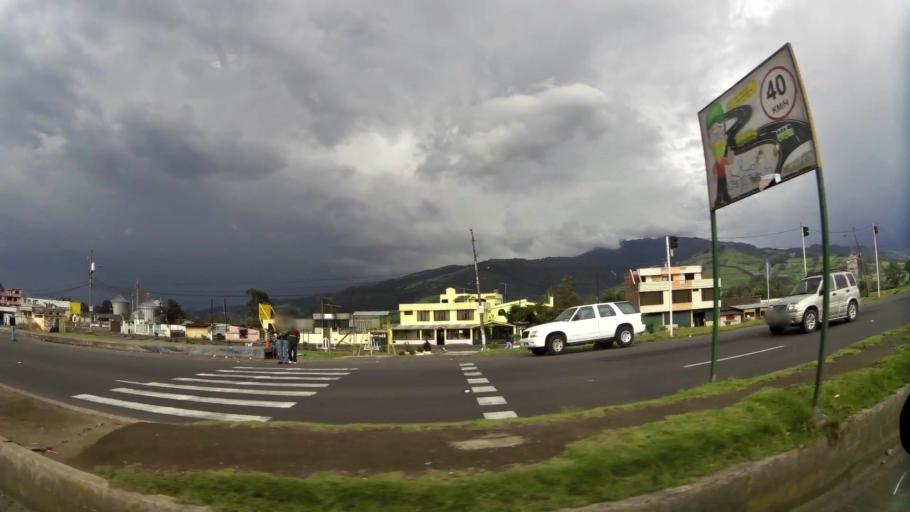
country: EC
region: Pichincha
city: Machachi
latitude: -0.4113
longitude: -78.5477
